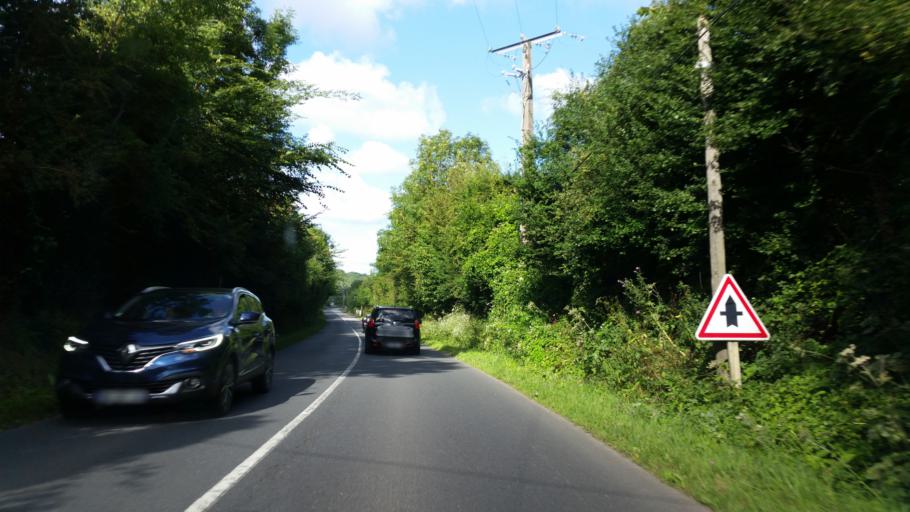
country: FR
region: Lower Normandy
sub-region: Departement du Calvados
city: Blonville-sur-Mer
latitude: 49.3193
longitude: 0.0574
